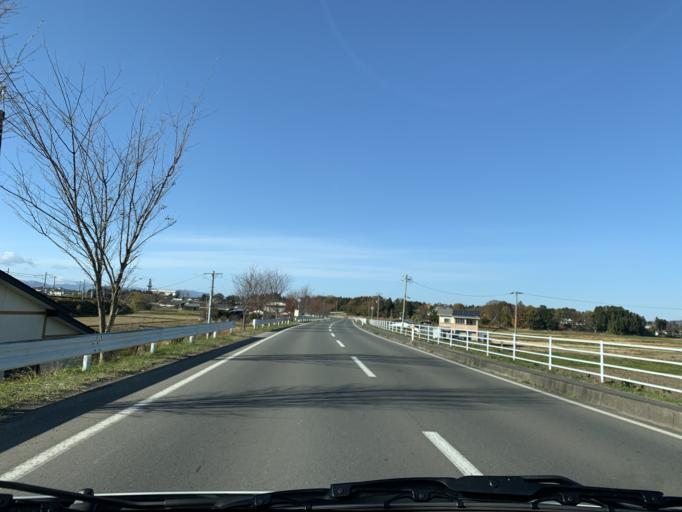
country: JP
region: Iwate
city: Mizusawa
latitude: 39.1881
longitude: 141.1258
